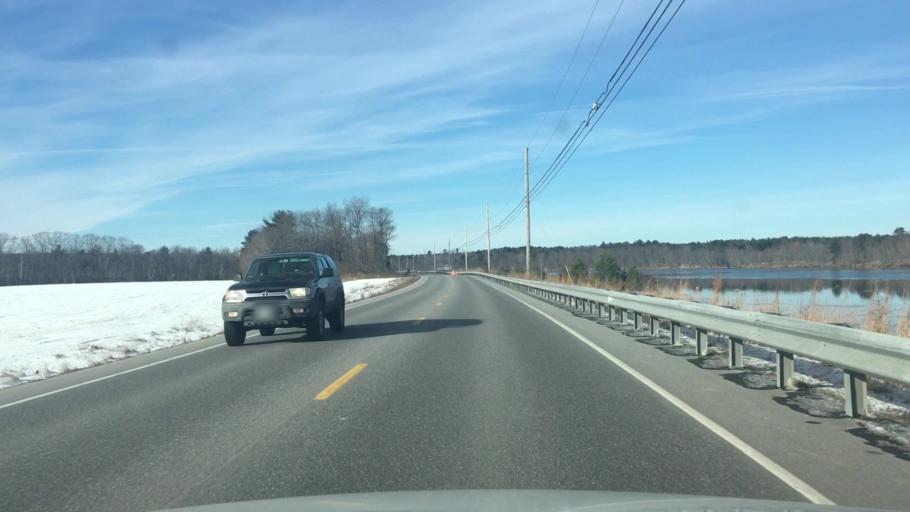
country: US
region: Maine
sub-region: Androscoggin County
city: Lisbon
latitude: 43.9912
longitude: -70.1395
